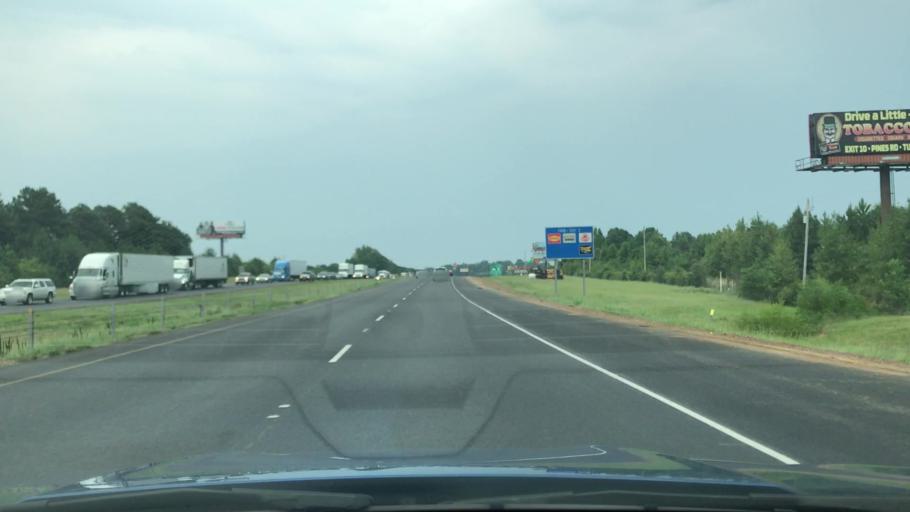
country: US
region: Louisiana
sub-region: Caddo Parish
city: Greenwood
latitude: 32.4504
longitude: -93.9932
